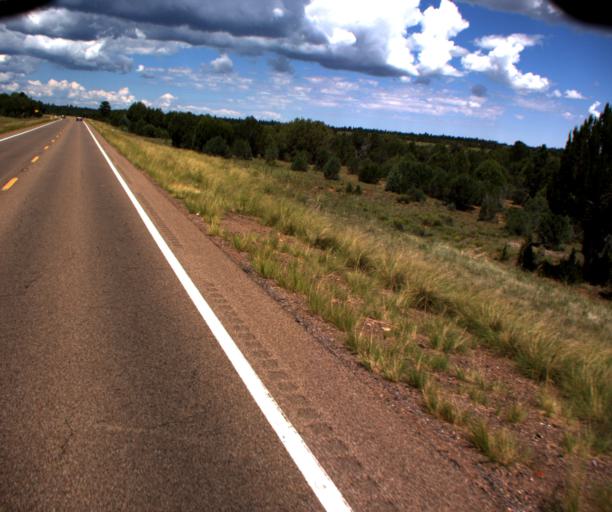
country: US
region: Arizona
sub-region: Navajo County
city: Heber-Overgaard
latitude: 34.3896
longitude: -110.5048
